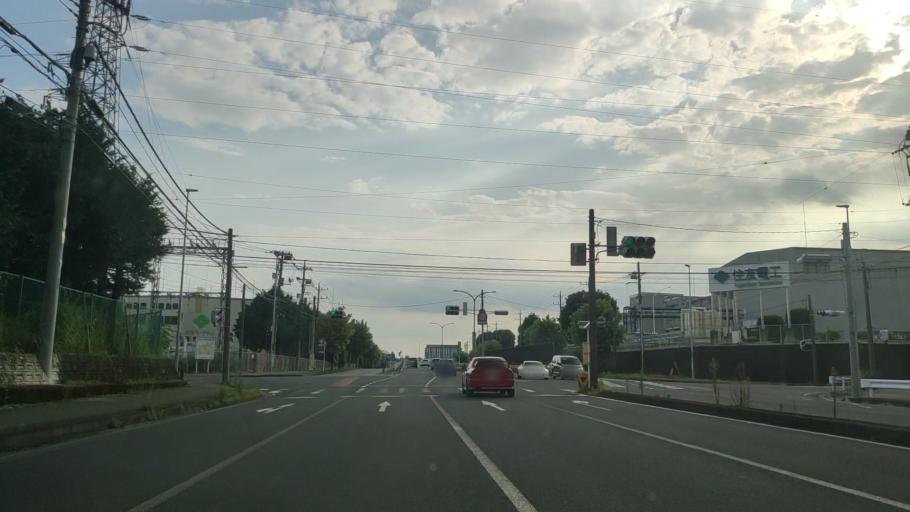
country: JP
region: Tochigi
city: Kanuma
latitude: 36.5382
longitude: 139.8101
